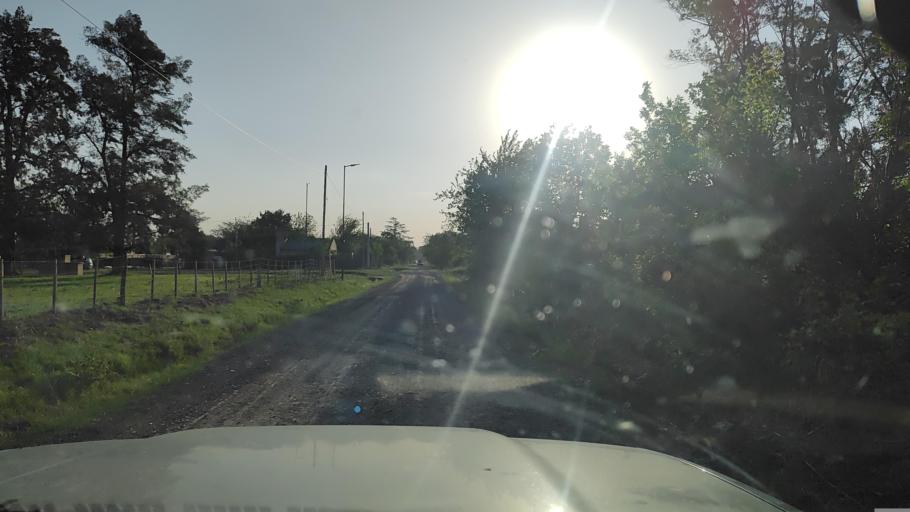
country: AR
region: Buenos Aires
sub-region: Partido de Lujan
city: Lujan
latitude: -34.5528
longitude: -59.2003
